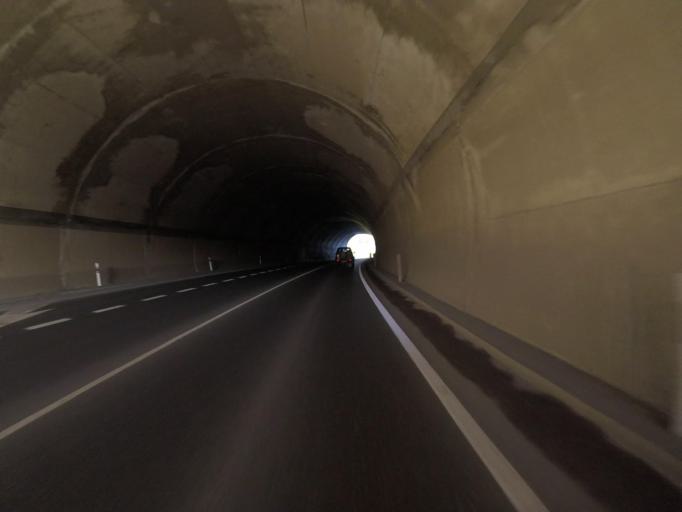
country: ES
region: Basque Country
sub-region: Provincia de Guipuzcoa
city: Astigarraga
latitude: 43.2874
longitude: -1.9395
